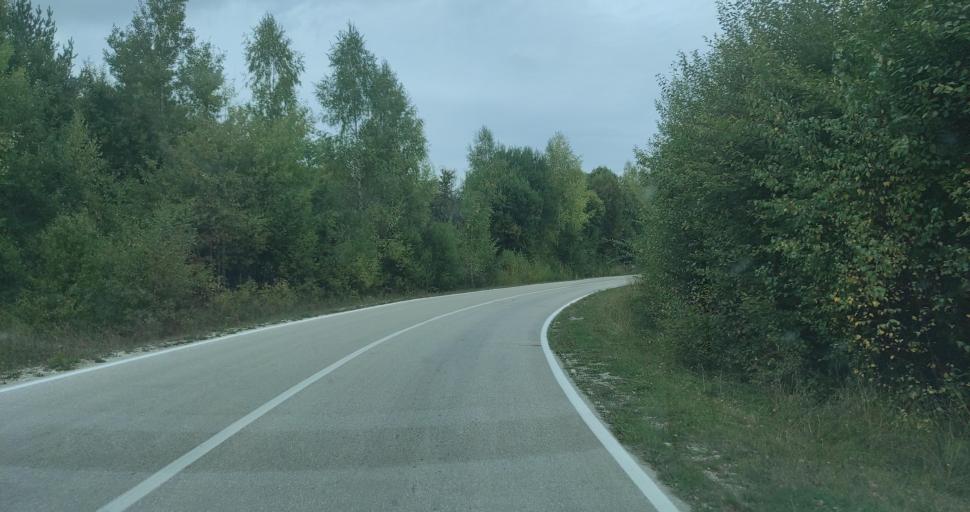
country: RS
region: Central Serbia
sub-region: Jablanicki Okrug
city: Crna Trava
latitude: 42.7037
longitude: 22.3266
